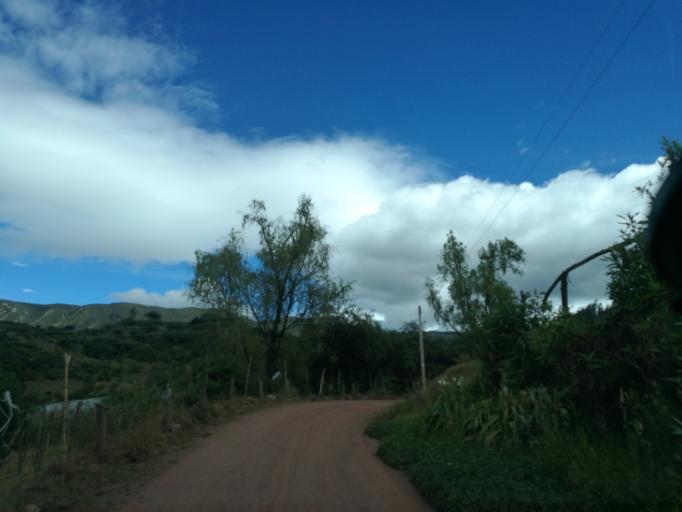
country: CO
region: Boyaca
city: Socota
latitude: 6.1098
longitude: -72.7169
